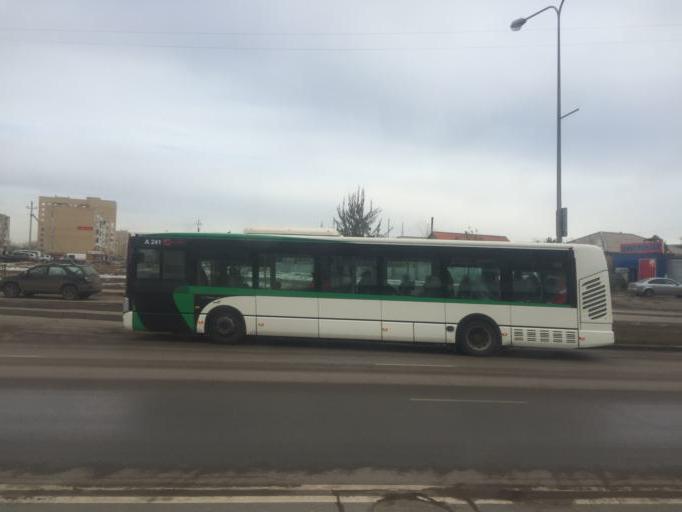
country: KZ
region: Astana Qalasy
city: Astana
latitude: 51.1696
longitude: 71.3886
